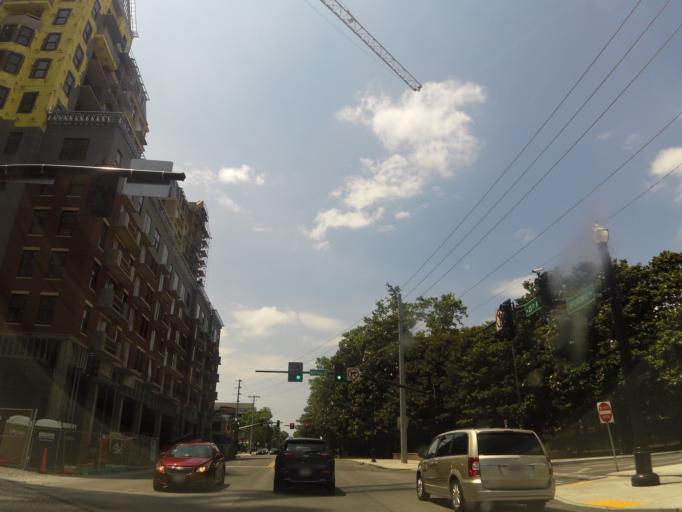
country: US
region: Tennessee
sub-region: Davidson County
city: Nashville
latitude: 36.1485
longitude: -86.7992
